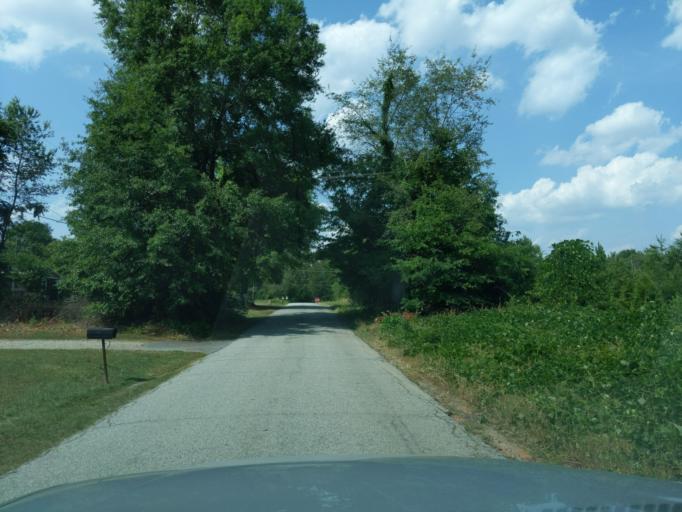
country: US
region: South Carolina
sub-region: Spartanburg County
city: Wellford
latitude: 34.9125
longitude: -82.0593
